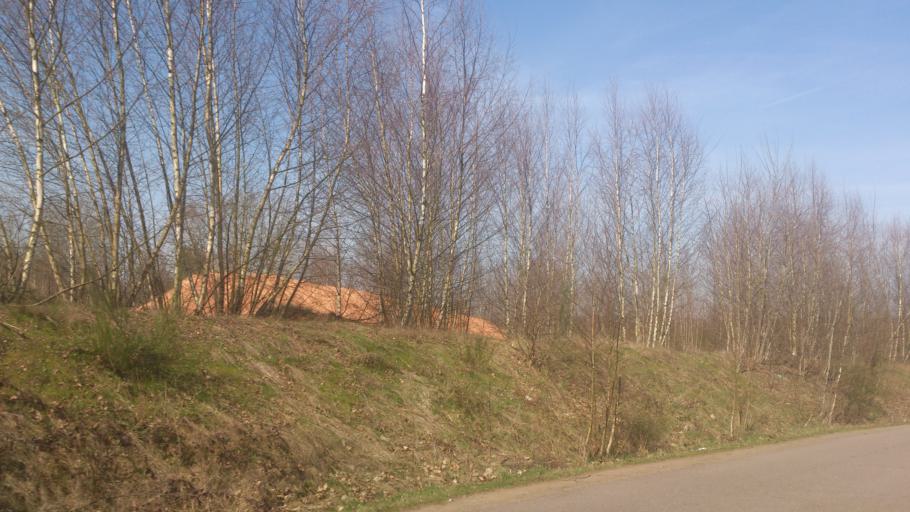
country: DE
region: Saarland
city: Bexbach
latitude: 49.3439
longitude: 7.2703
